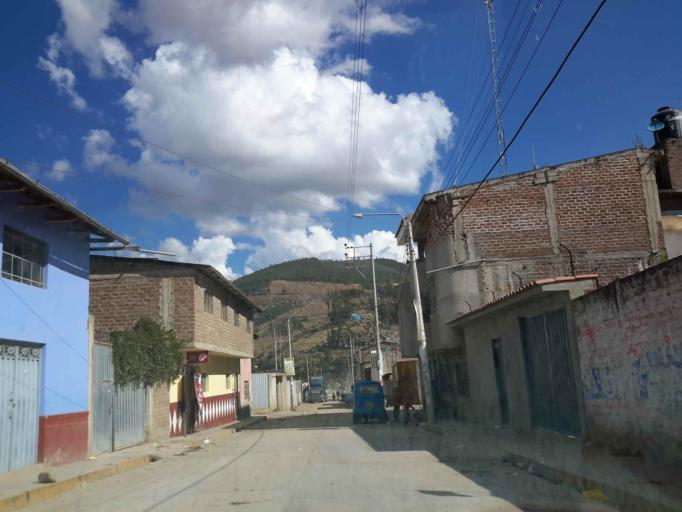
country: PE
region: Apurimac
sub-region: Provincia de Andahuaylas
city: Talavera
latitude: -13.6537
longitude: -73.4311
